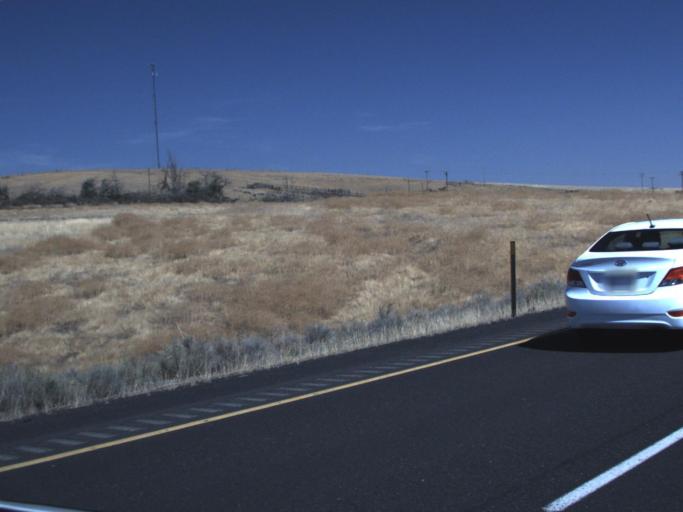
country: US
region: Washington
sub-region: Grant County
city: Warden
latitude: 47.0852
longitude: -118.9438
